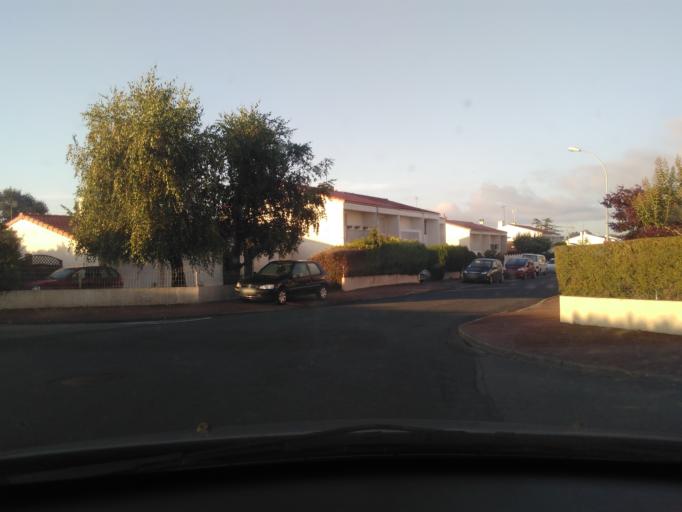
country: FR
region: Pays de la Loire
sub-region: Departement de la Vendee
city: Mouilleron-le-Captif
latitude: 46.7267
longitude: -1.4214
